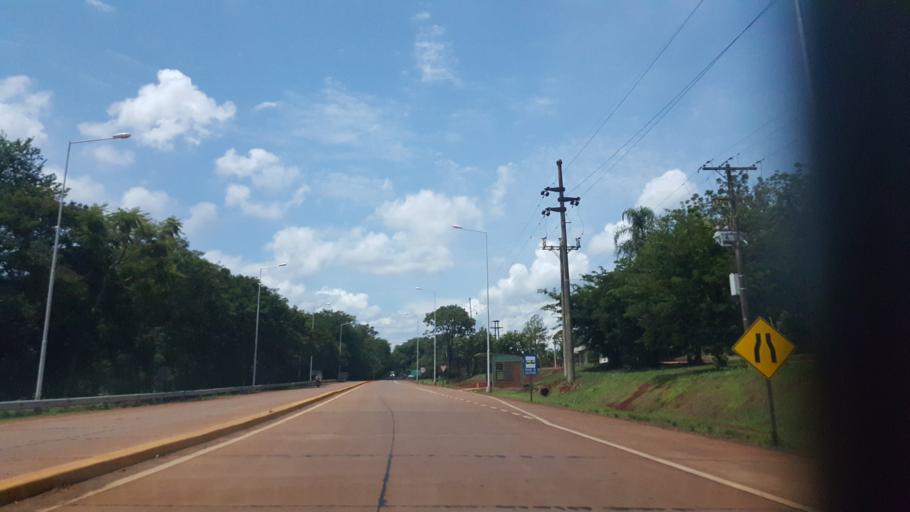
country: AR
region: Misiones
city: Puerto Rico
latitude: -26.8208
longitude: -55.0220
